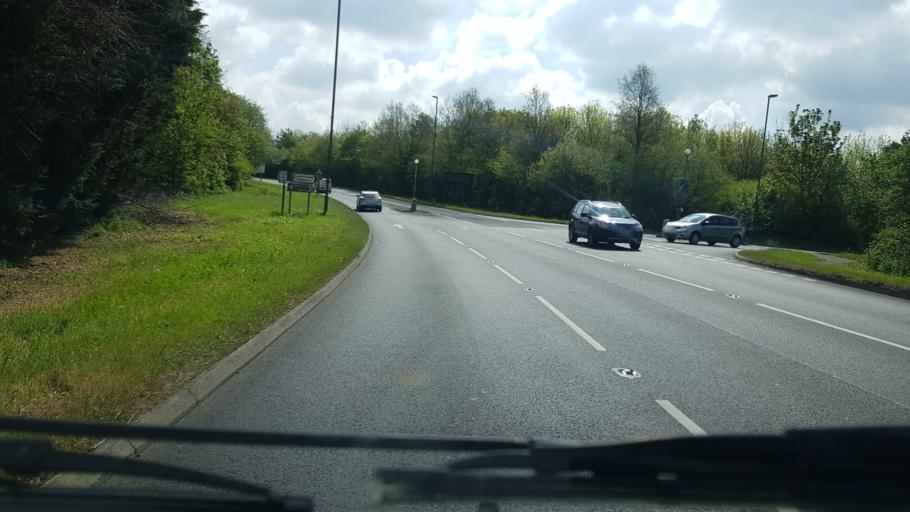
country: GB
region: England
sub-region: Surrey
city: Leatherhead
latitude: 51.3165
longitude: -0.3352
